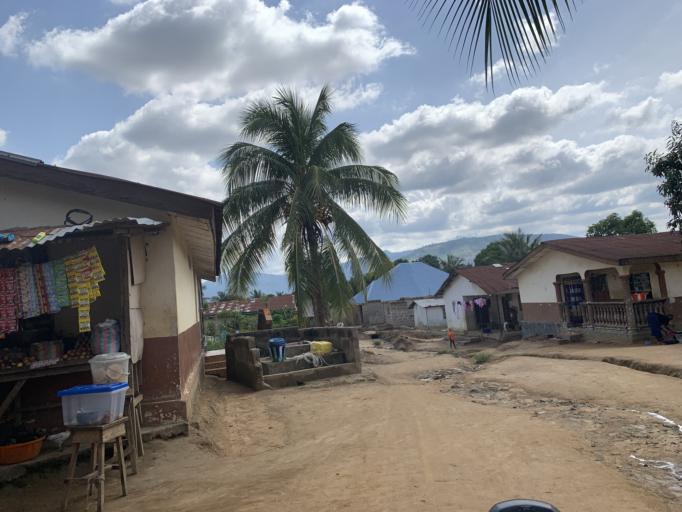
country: SL
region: Western Area
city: Waterloo
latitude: 8.3360
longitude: -13.0503
